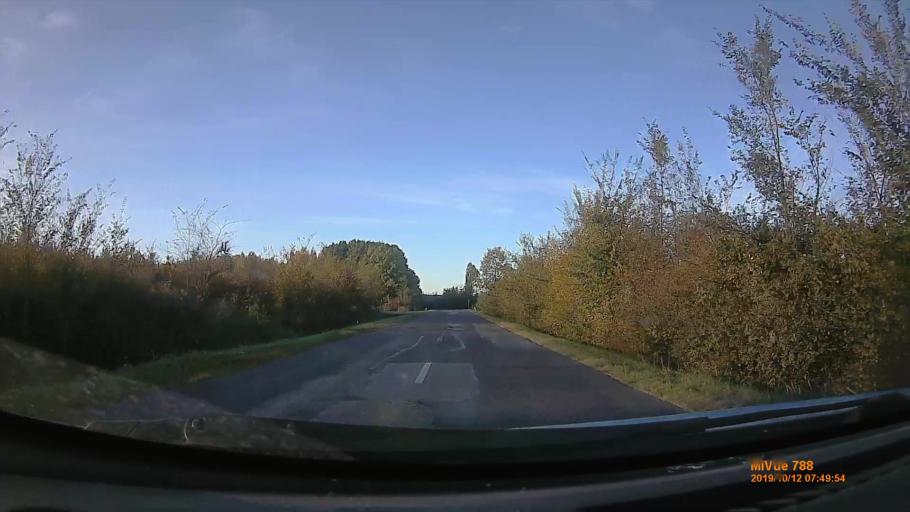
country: HU
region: Hajdu-Bihar
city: Biharkeresztes
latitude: 47.1580
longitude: 21.7415
